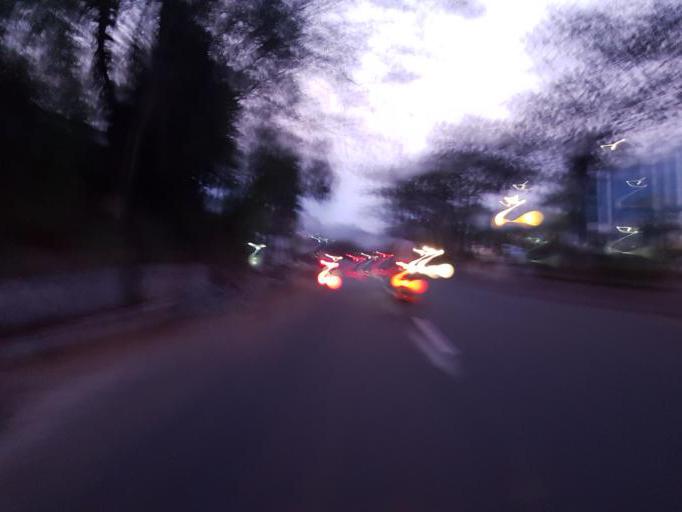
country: ID
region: West Java
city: Serpong
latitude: -6.3316
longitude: 106.6780
